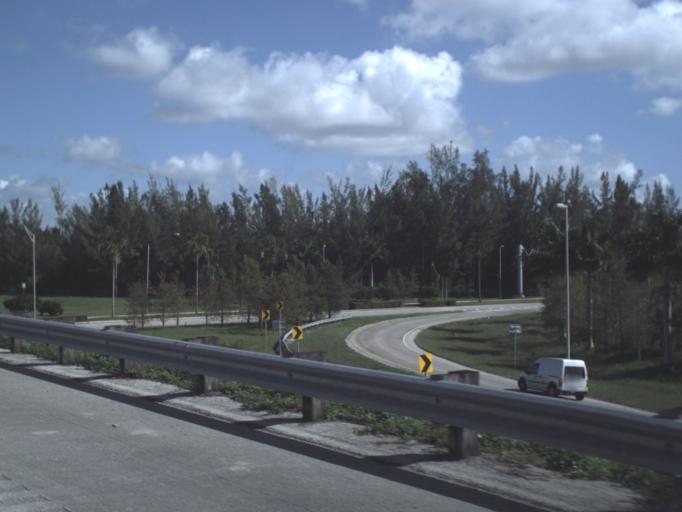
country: US
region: Florida
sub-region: Broward County
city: Coral Springs
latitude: 26.2720
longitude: -80.2964
